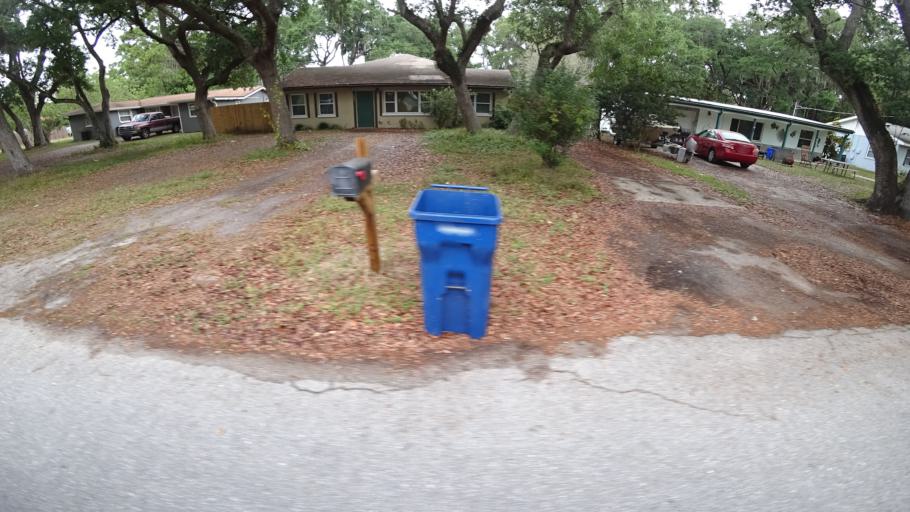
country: US
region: Florida
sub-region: Manatee County
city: South Bradenton
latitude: 27.4490
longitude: -82.5862
